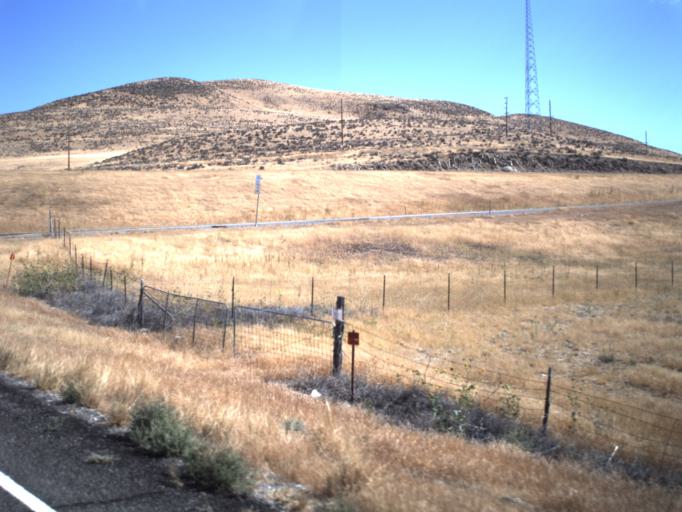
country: US
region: Utah
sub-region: Box Elder County
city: Garland
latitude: 41.8158
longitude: -112.4132
